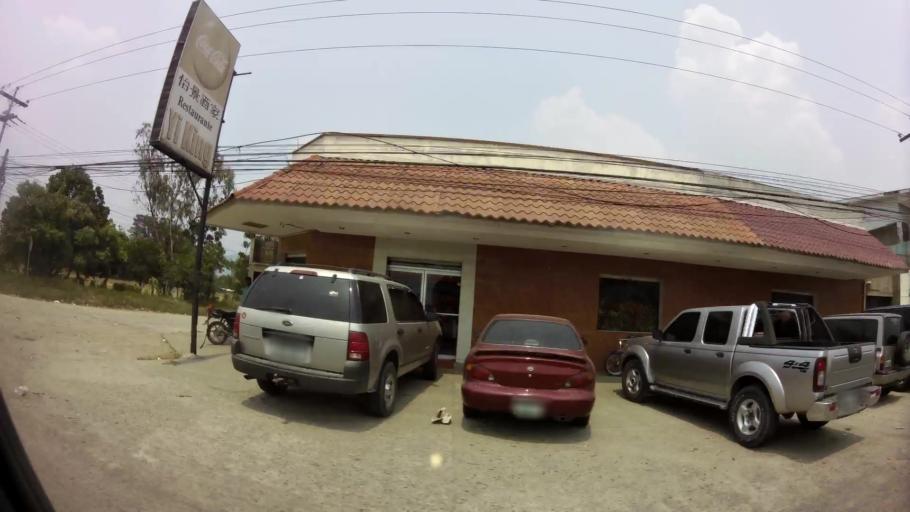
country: HN
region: Yoro
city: El Progreso
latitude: 15.3900
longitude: -87.8060
